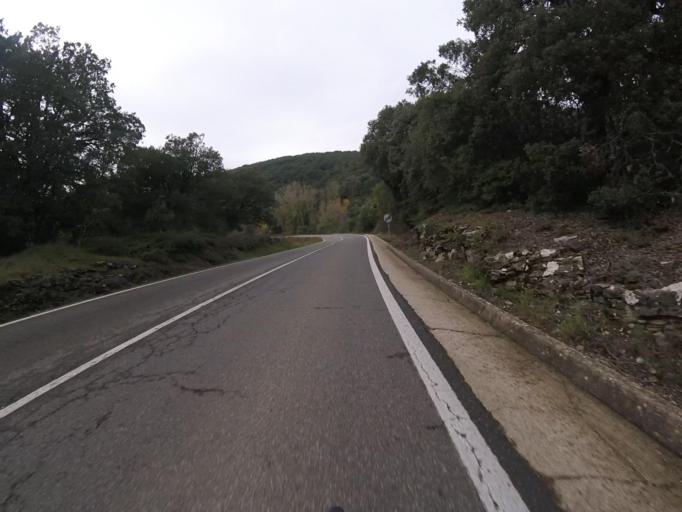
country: ES
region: Navarre
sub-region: Provincia de Navarra
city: Lezaun
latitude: 42.7541
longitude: -2.0150
